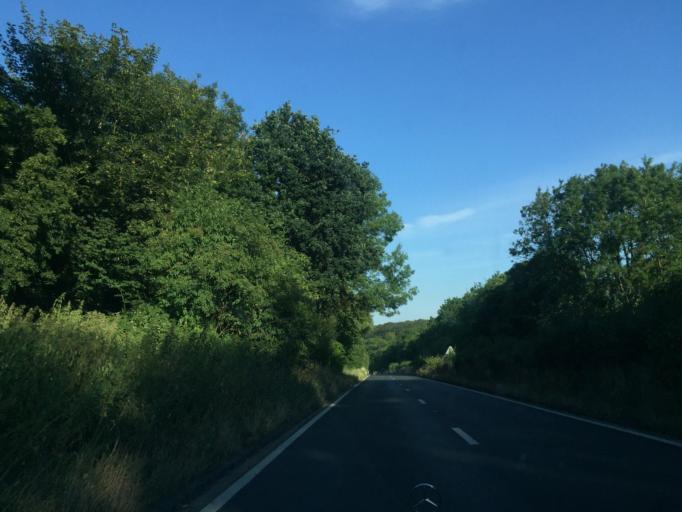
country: GB
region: England
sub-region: Oxfordshire
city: Rotherfield Peppard
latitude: 51.5591
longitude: -0.9484
